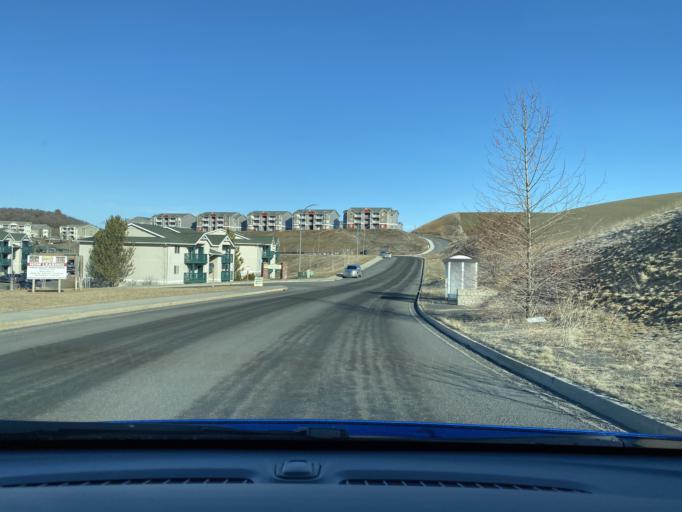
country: US
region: Washington
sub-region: Whitman County
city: Pullman
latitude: 46.7462
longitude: -117.1453
